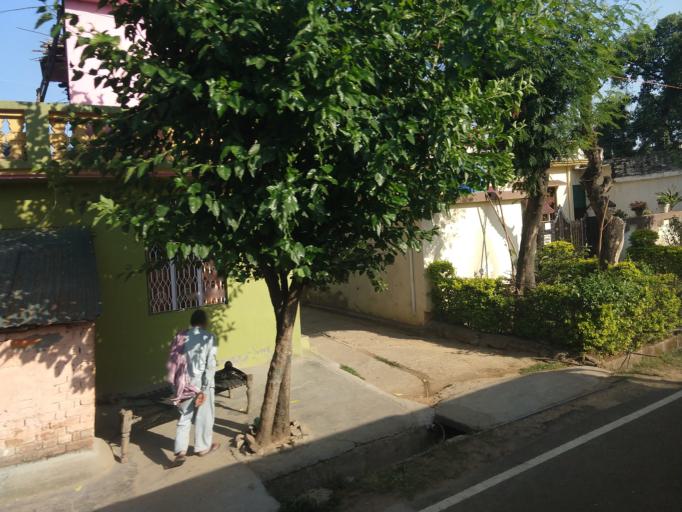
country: IN
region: Himachal Pradesh
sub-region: Chamba
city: Chowari
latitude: 32.3560
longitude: 75.9196
